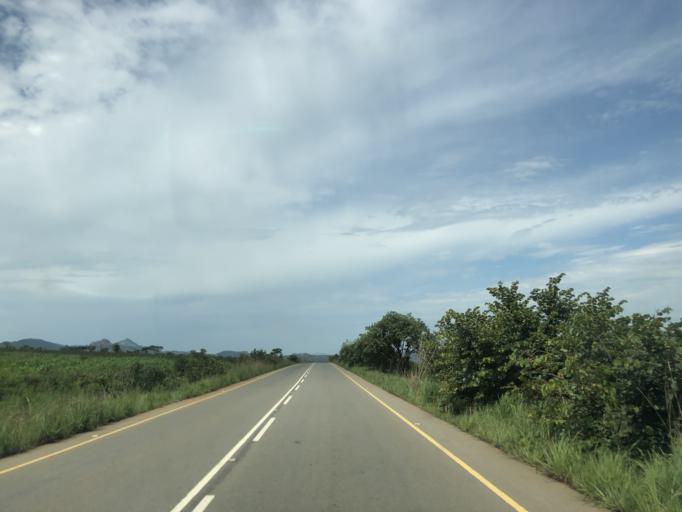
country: AO
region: Cuanza Sul
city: Quibala
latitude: -10.7331
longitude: 15.0192
